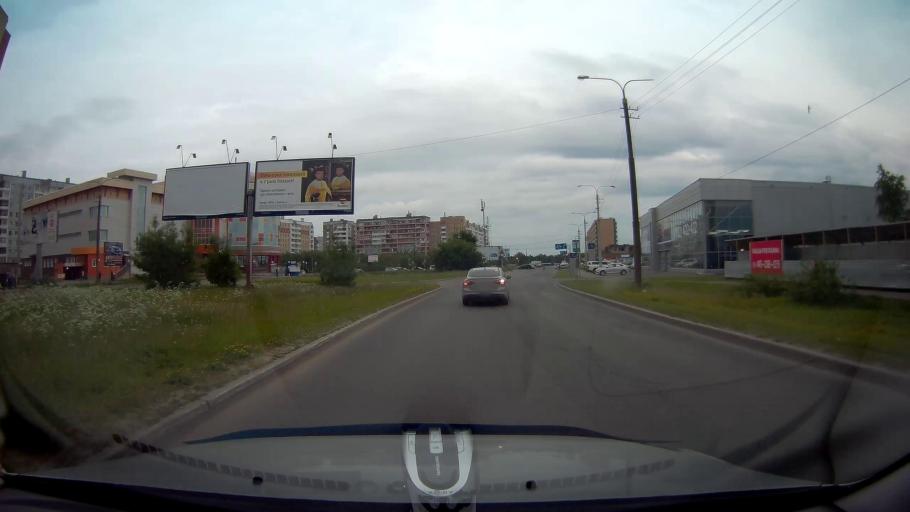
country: RU
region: Arkhangelskaya
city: Arkhangel'sk
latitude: 64.5320
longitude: 40.6143
